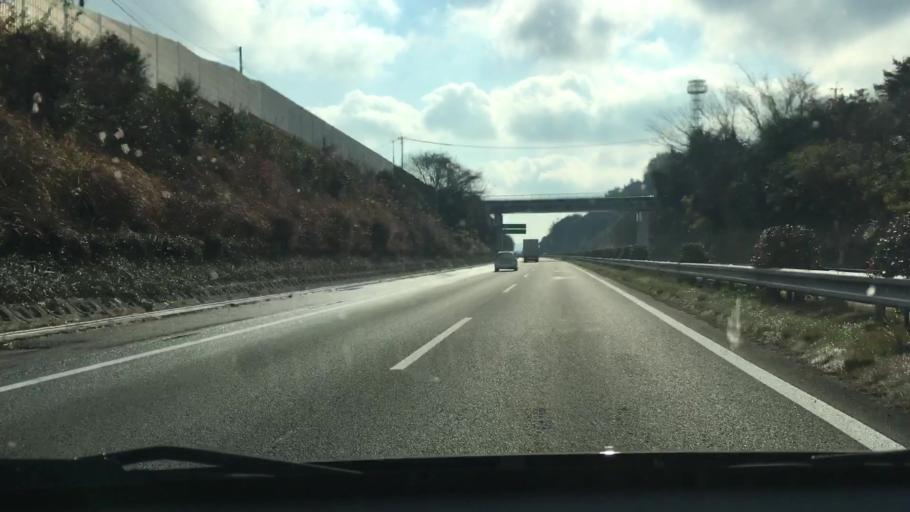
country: JP
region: Kumamoto
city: Kumamoto
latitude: 32.7290
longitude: 130.7741
